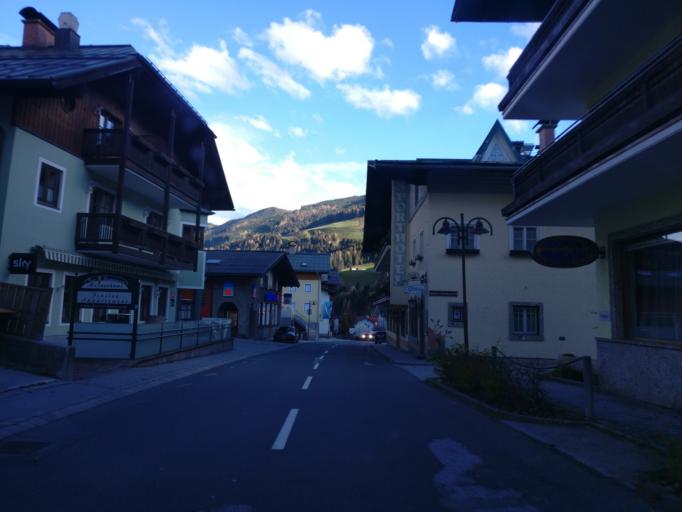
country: AT
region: Salzburg
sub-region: Politischer Bezirk Sankt Johann im Pongau
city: Muhlbach am Hochkonig
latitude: 47.3770
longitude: 13.1251
